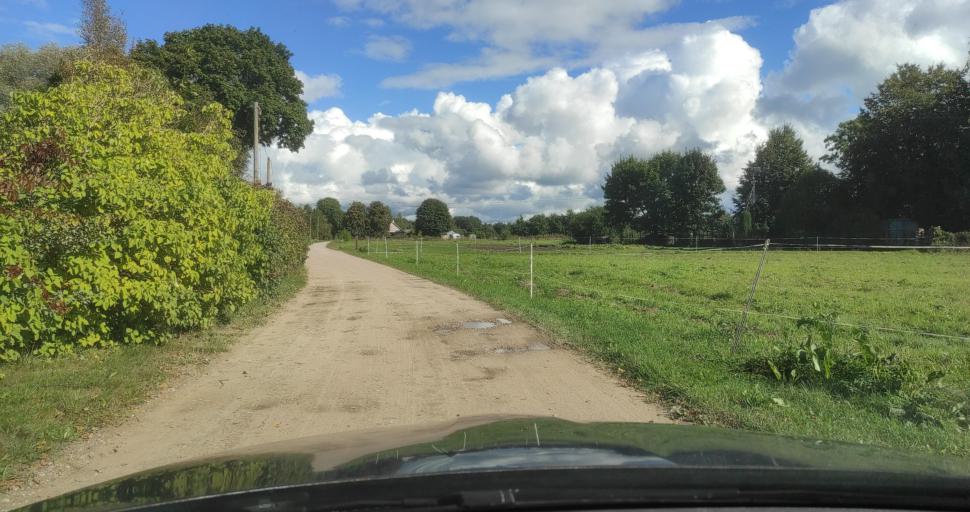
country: LV
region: Ventspils
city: Ventspils
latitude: 57.3661
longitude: 21.6228
